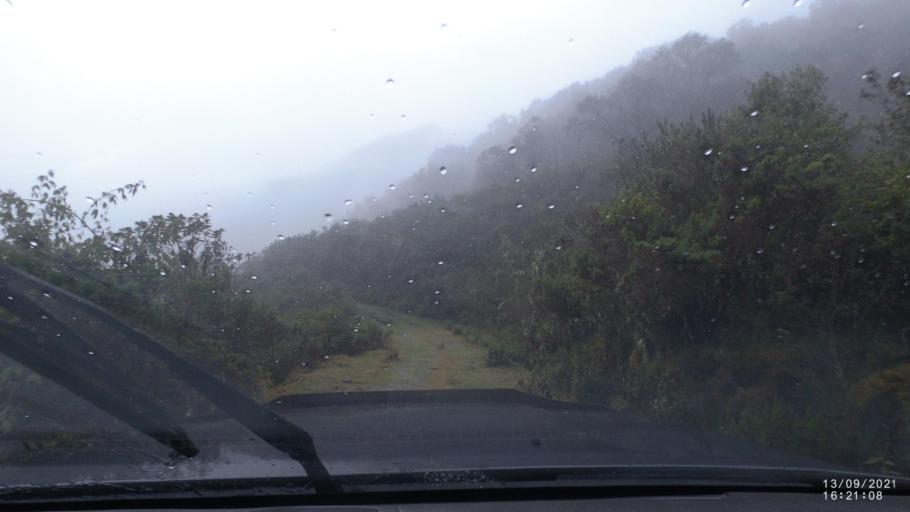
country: BO
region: Cochabamba
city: Colomi
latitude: -17.2687
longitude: -65.7026
